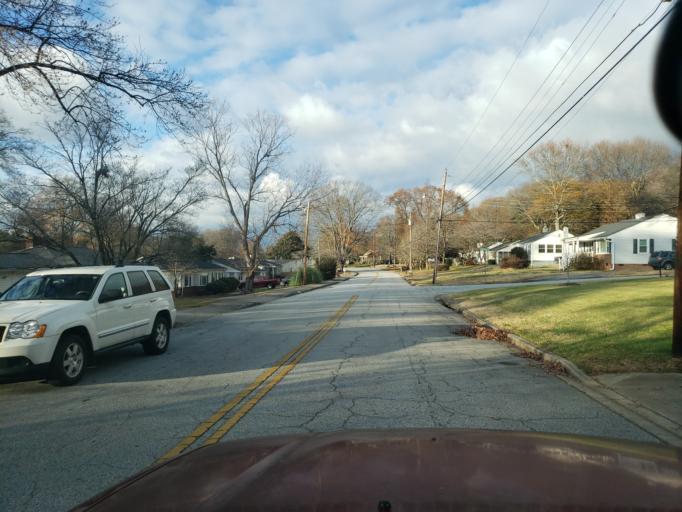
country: US
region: South Carolina
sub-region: Greenville County
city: Greenville
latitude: 34.8311
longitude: -82.3636
